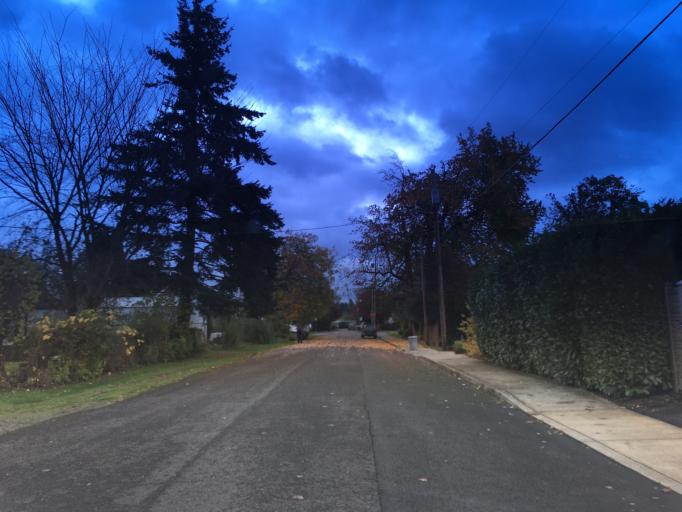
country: US
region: Oregon
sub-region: Multnomah County
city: Fairview
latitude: 45.5379
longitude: -122.4363
